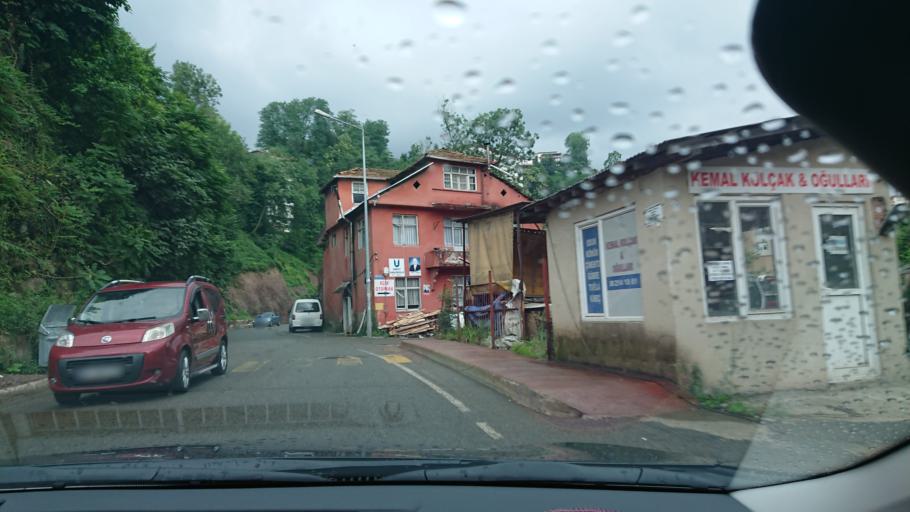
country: TR
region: Rize
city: Rize
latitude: 41.0263
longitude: 40.5128
